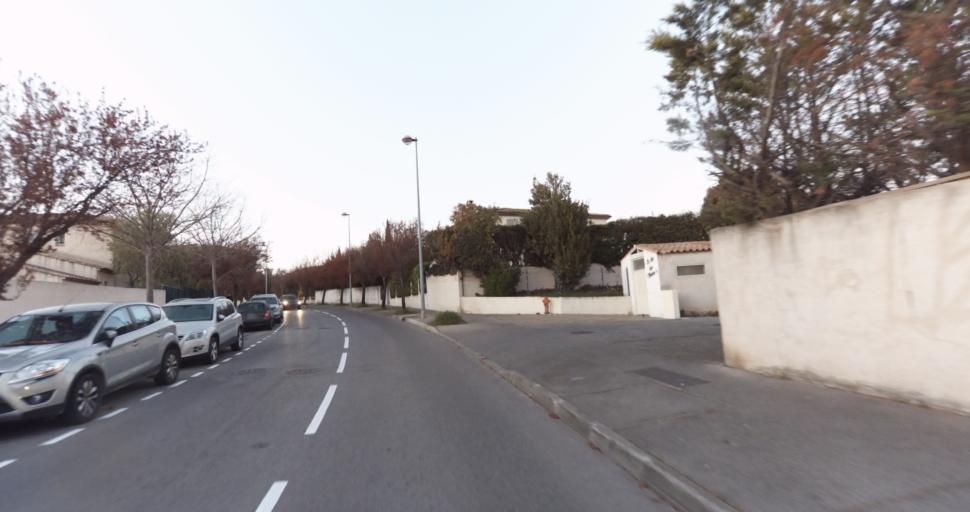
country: FR
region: Provence-Alpes-Cote d'Azur
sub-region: Departement des Bouches-du-Rhone
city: Aix-en-Provence
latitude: 43.5331
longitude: 5.4108
